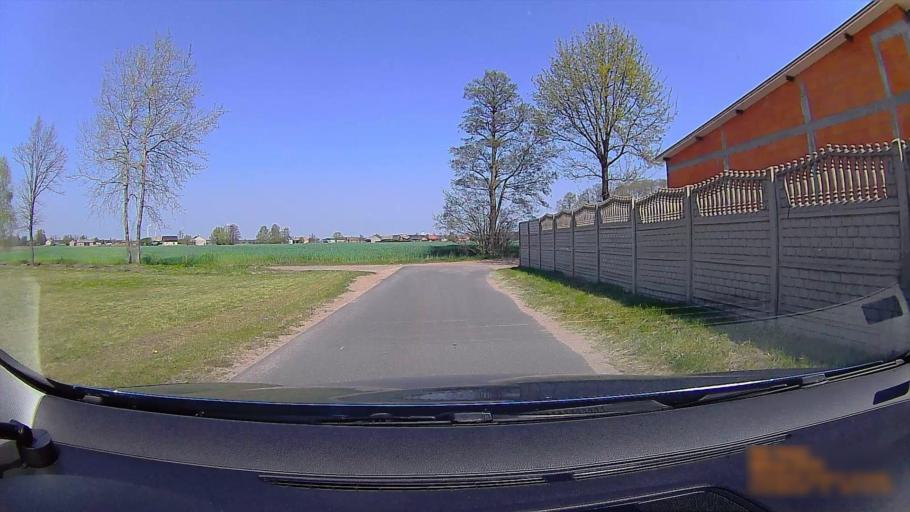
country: PL
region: Greater Poland Voivodeship
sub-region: Powiat koninski
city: Rychwal
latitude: 52.1014
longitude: 18.1850
